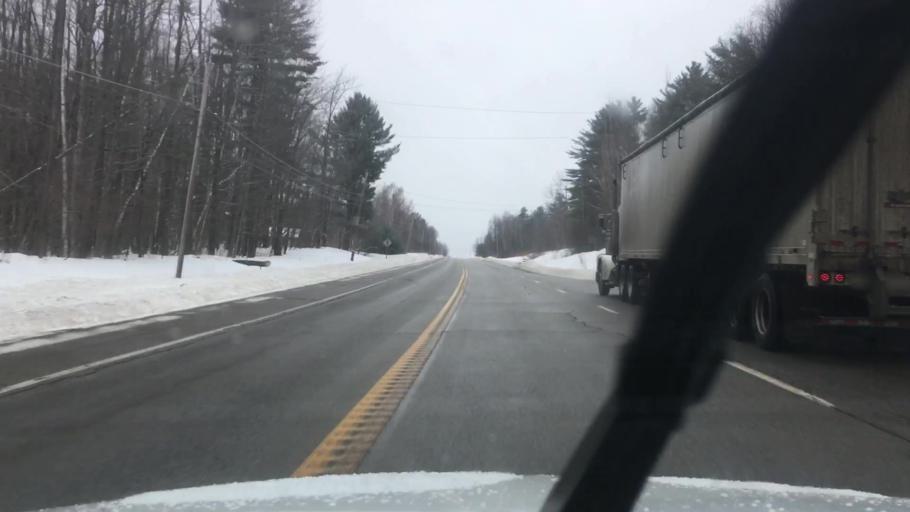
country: US
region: Maine
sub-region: Oxford County
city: Peru
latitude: 44.5754
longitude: -70.3705
